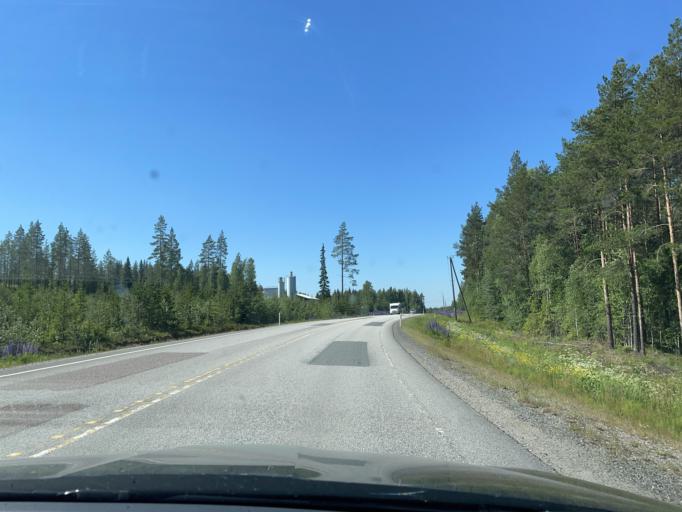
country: FI
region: Central Finland
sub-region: Saarijaervi-Viitasaari
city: Viitasaari
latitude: 63.1397
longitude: 25.7814
